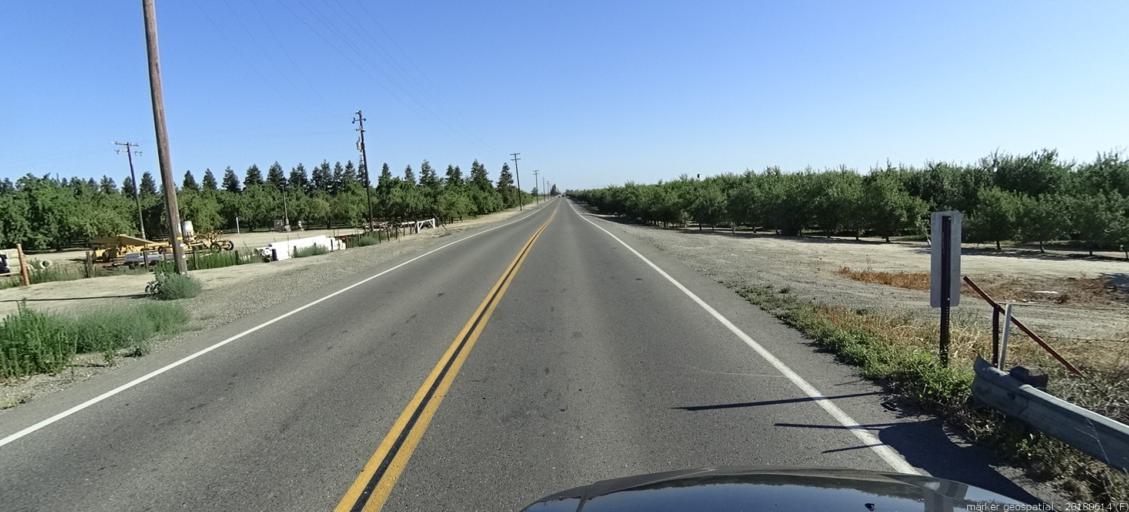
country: US
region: California
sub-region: Madera County
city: Madera
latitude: 36.9681
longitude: -120.1285
